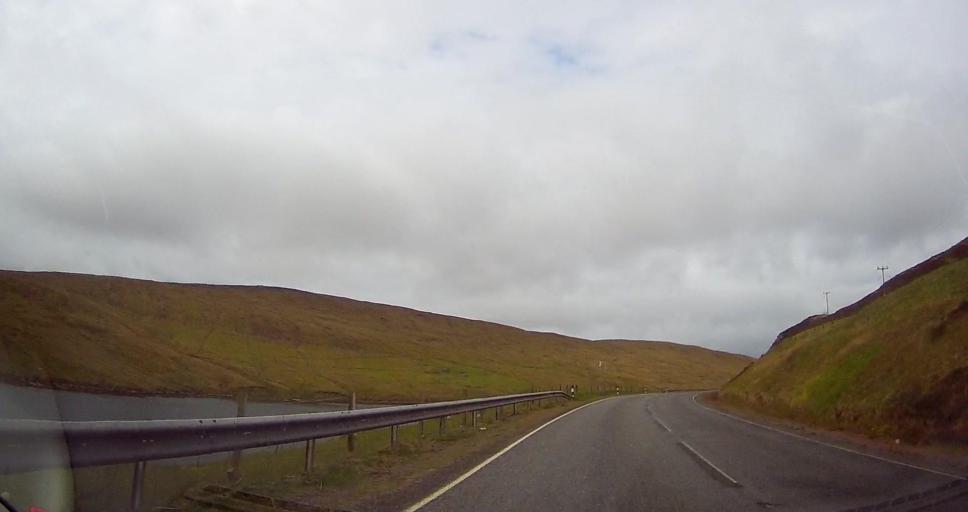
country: GB
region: Scotland
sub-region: Shetland Islands
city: Lerwick
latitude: 60.3561
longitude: -1.2753
